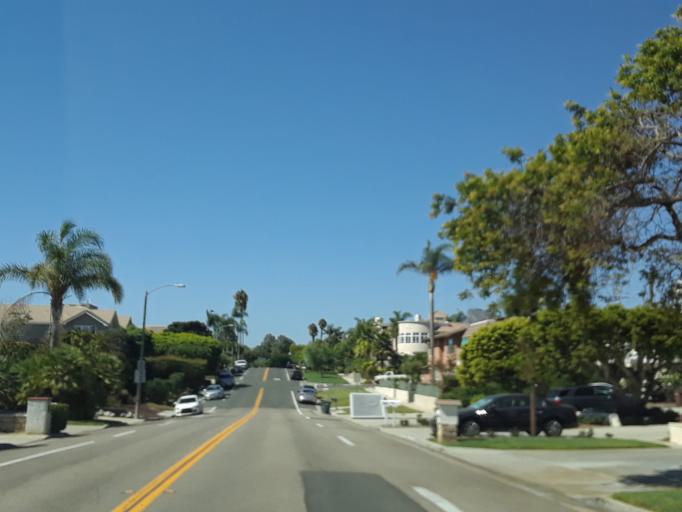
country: US
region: California
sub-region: Orange County
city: Dana Point
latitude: 33.4599
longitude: -117.6723
